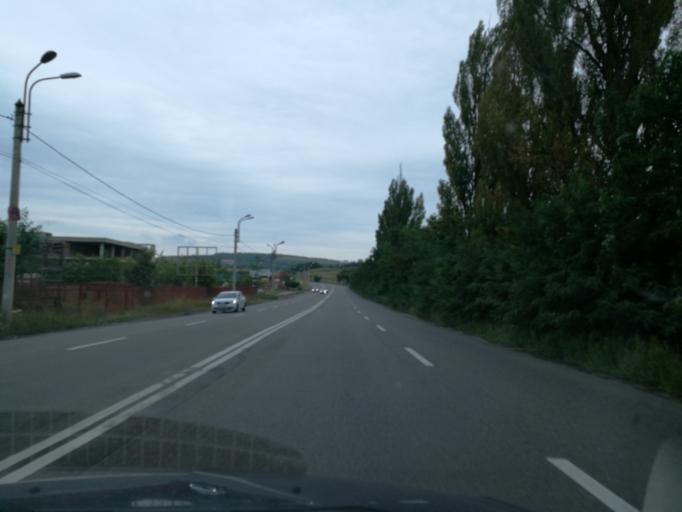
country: RO
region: Suceava
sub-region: Municipiul Falticeni
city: Falticeni
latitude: 47.4805
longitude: 26.2918
